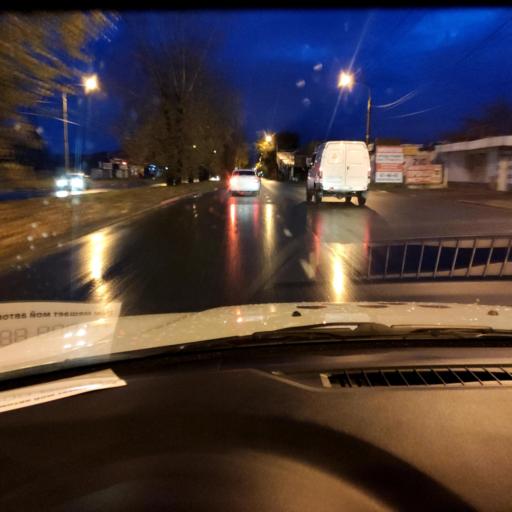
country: RU
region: Samara
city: Tol'yatti
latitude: 53.5166
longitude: 49.4313
